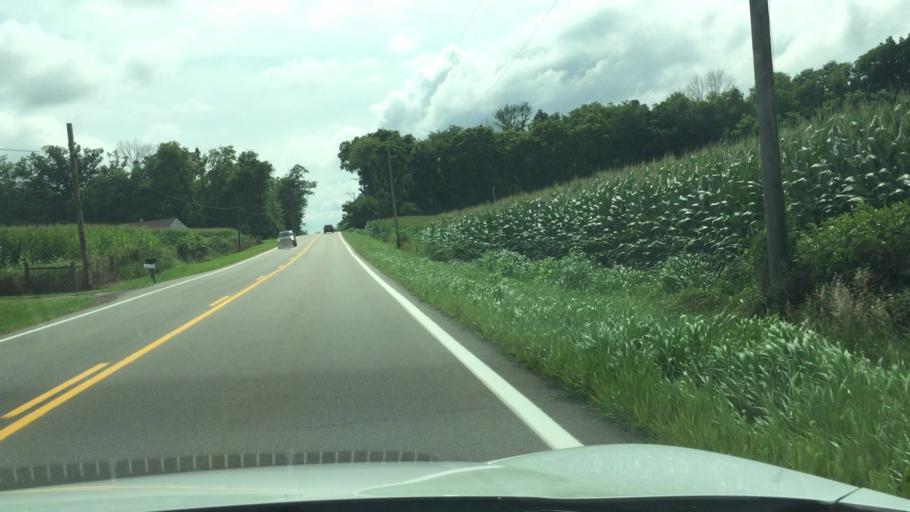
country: US
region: Ohio
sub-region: Clark County
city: Northridge
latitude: 40.0146
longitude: -83.6873
